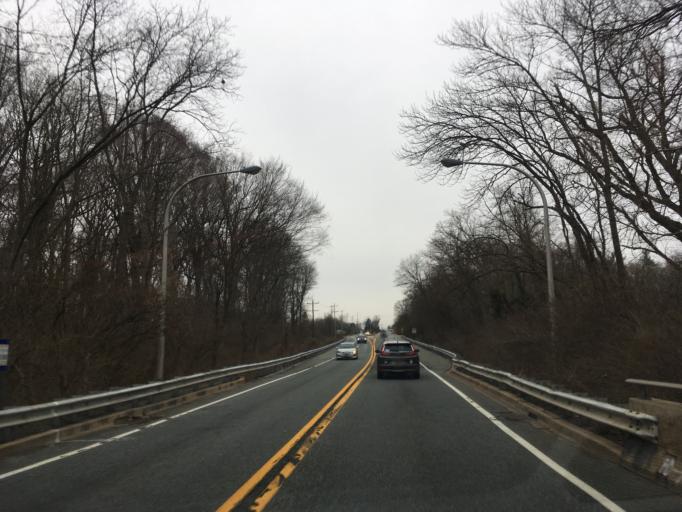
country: US
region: Delaware
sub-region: New Castle County
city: Greenville
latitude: 39.7732
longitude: -75.5798
